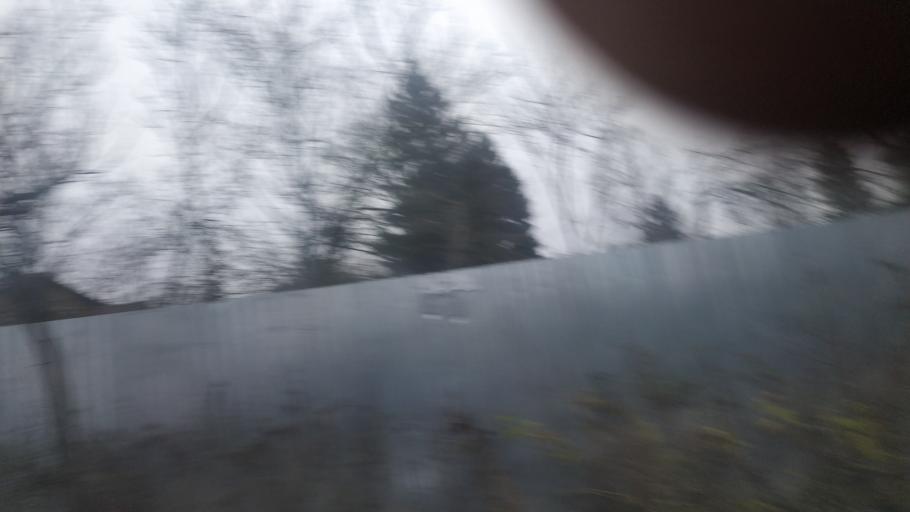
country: RU
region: Moskovskaya
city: Lugovaya
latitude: 56.0543
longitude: 37.4762
